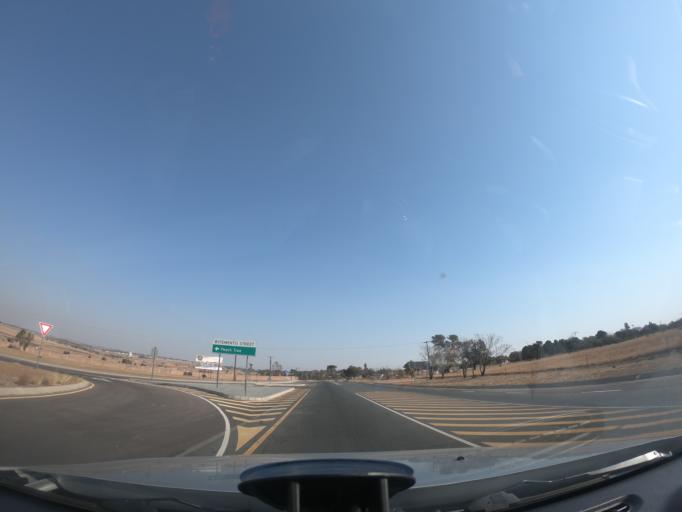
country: ZA
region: Gauteng
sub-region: City of Johannesburg Metropolitan Municipality
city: Diepsloot
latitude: -25.8733
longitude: 28.0289
